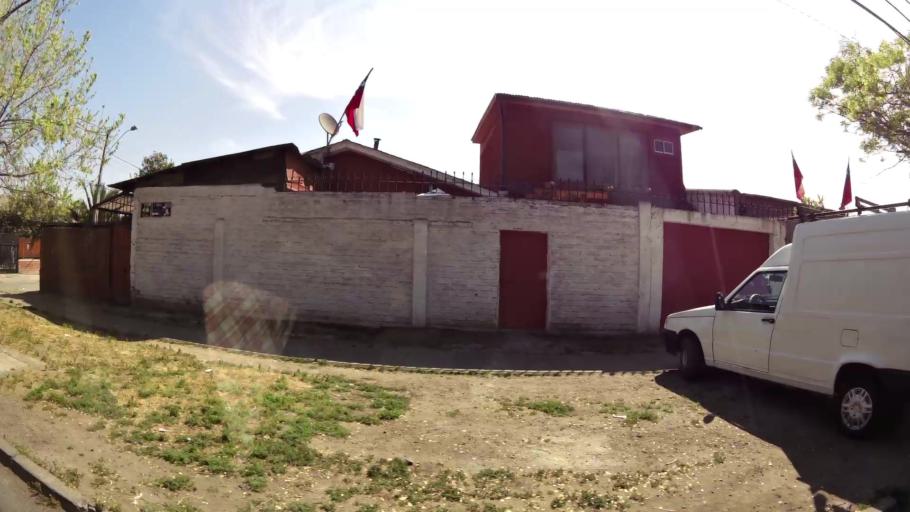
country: CL
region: Santiago Metropolitan
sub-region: Provincia de Santiago
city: Santiago
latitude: -33.3979
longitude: -70.6543
